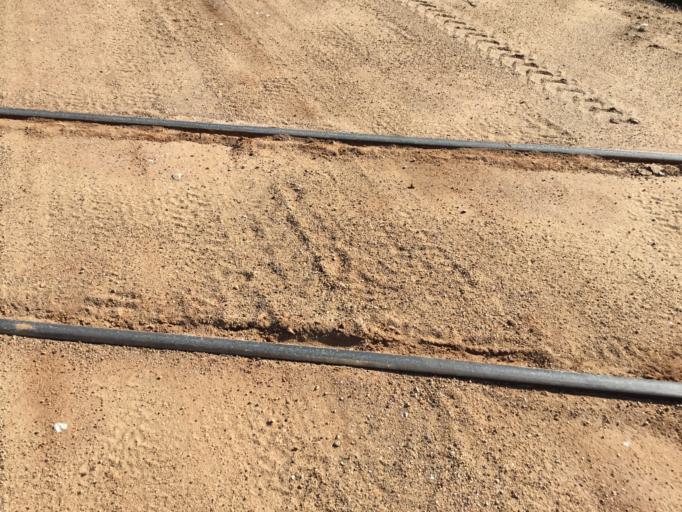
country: US
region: Kansas
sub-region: Kingman County
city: Kingman
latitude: 37.5355
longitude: -98.0089
